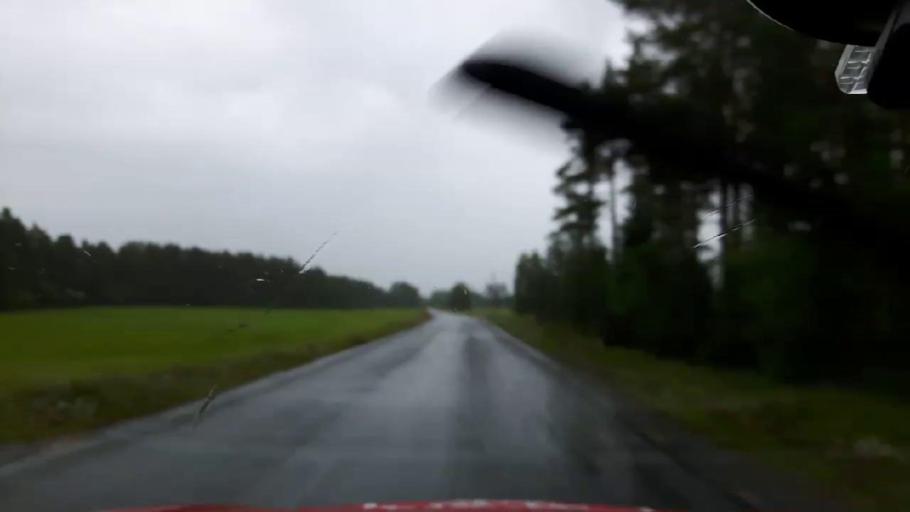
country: SE
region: Jaemtland
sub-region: OEstersunds Kommun
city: Brunflo
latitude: 62.9976
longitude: 14.7664
